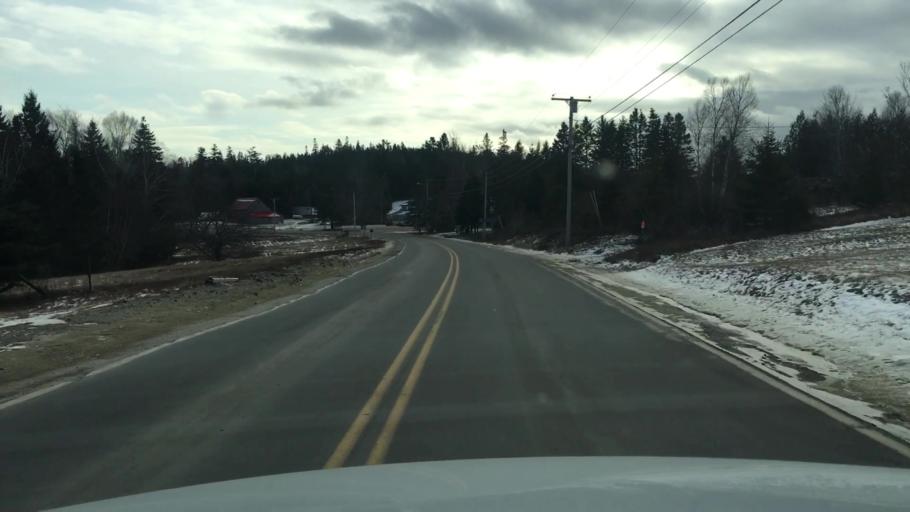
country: US
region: Maine
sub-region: Washington County
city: Jonesport
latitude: 44.6187
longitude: -67.6065
